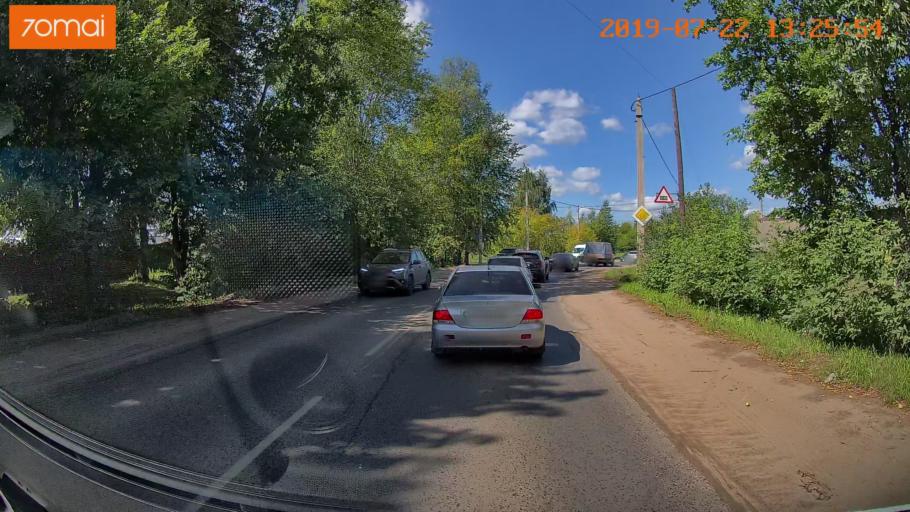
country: RU
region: Ivanovo
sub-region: Gorod Ivanovo
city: Ivanovo
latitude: 57.0278
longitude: 40.9489
